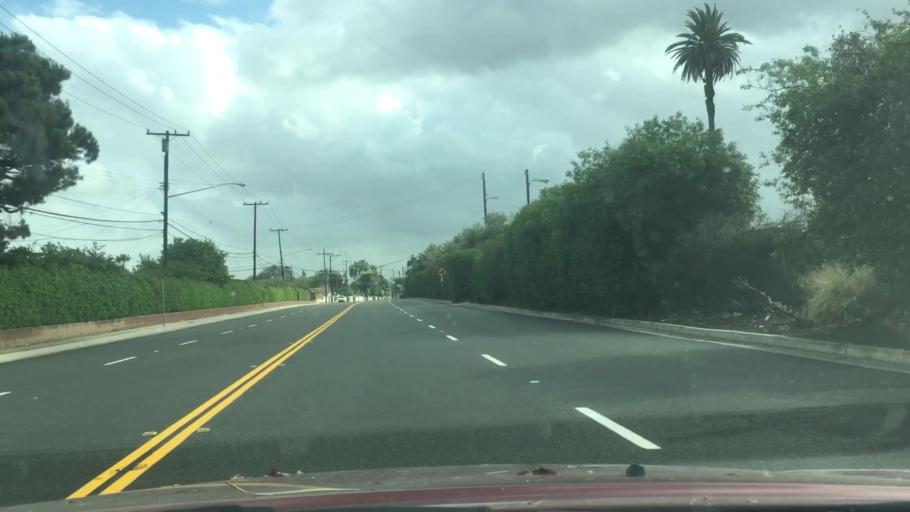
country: US
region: California
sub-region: Los Angeles County
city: La Mirada
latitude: 33.8959
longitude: -118.0253
